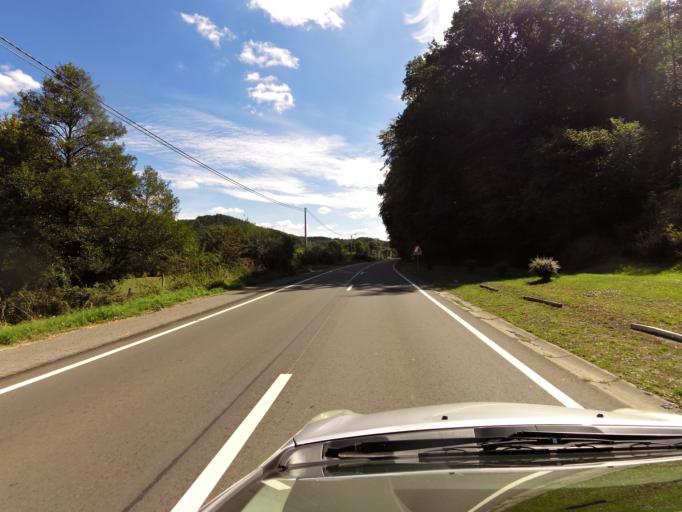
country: BE
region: Wallonia
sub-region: Province du Luxembourg
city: Rendeux
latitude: 50.2539
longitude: 5.4816
